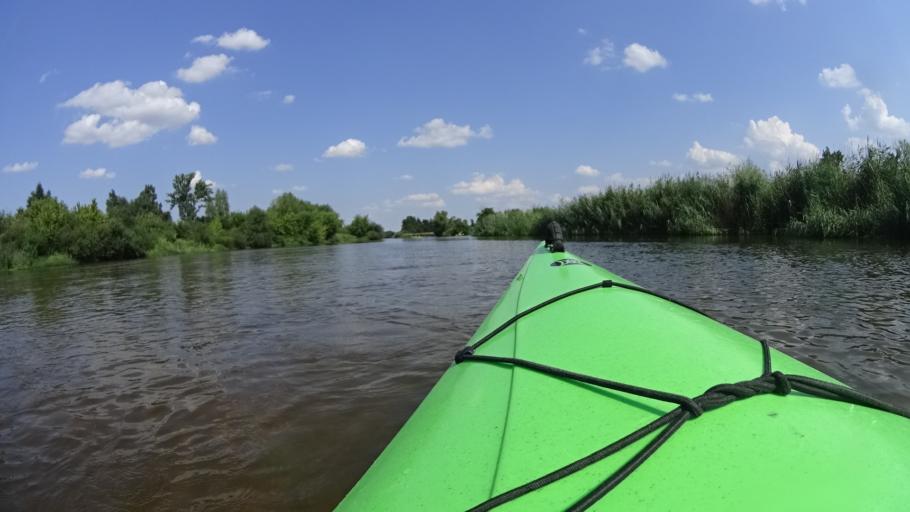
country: PL
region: Masovian Voivodeship
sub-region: Powiat bialobrzeski
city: Wysmierzyce
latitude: 51.6557
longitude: 20.8277
